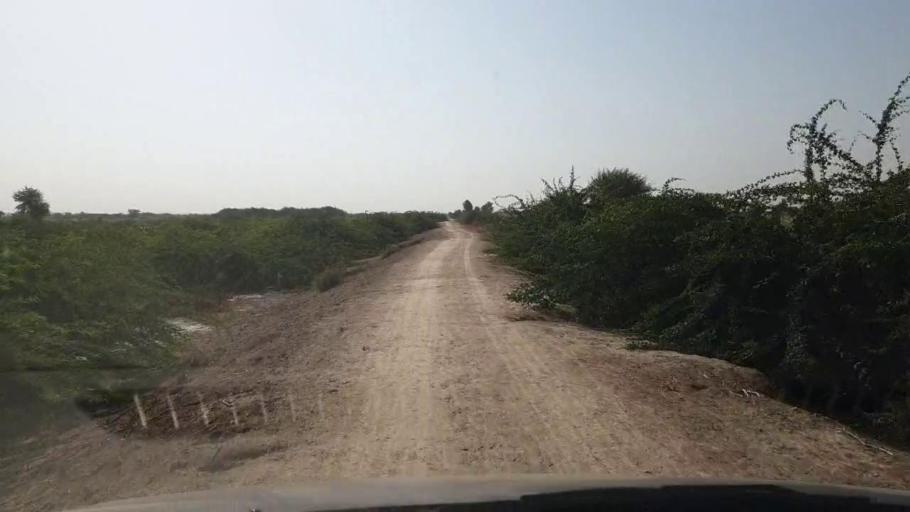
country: PK
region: Sindh
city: Kadhan
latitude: 24.5742
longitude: 69.0816
